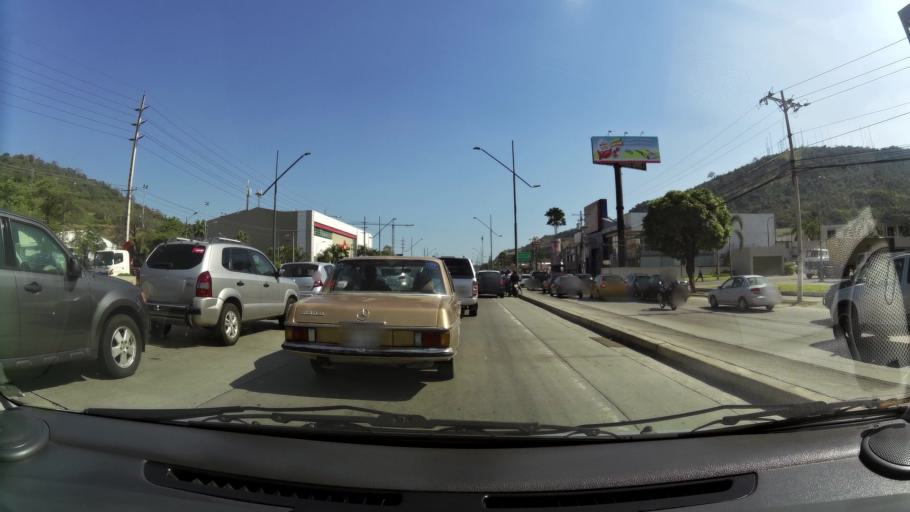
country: EC
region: Guayas
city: Guayaquil
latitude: -2.1718
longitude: -79.9394
